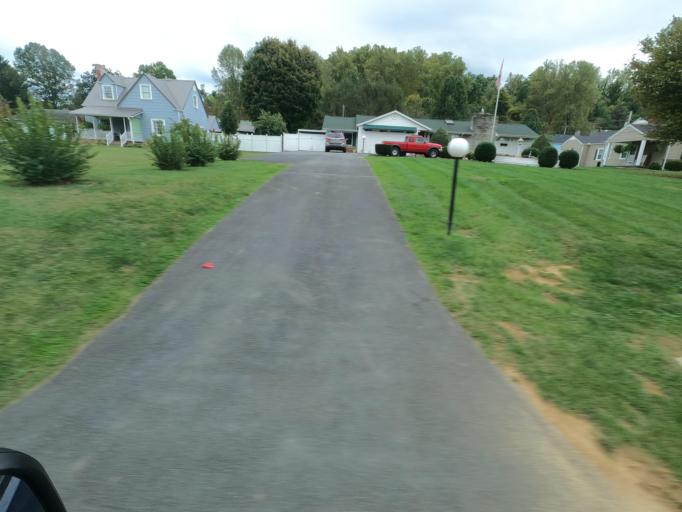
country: US
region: Tennessee
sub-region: Carter County
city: Elizabethton
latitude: 36.3403
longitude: -82.2504
